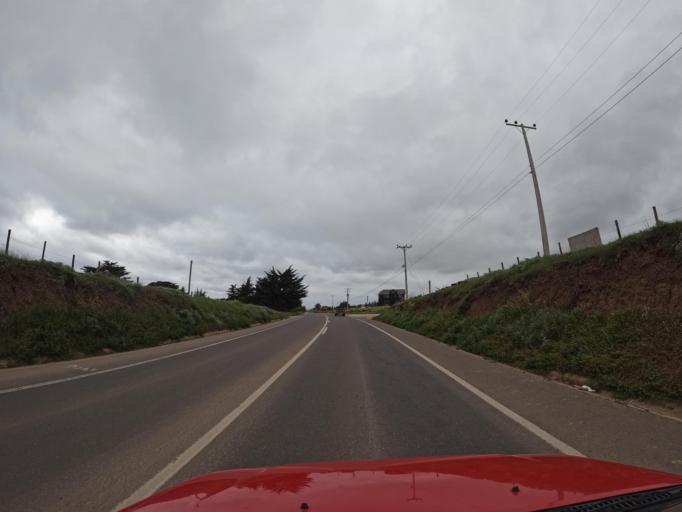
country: CL
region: O'Higgins
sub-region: Provincia de Colchagua
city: Santa Cruz
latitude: -34.4390
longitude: -72.0325
